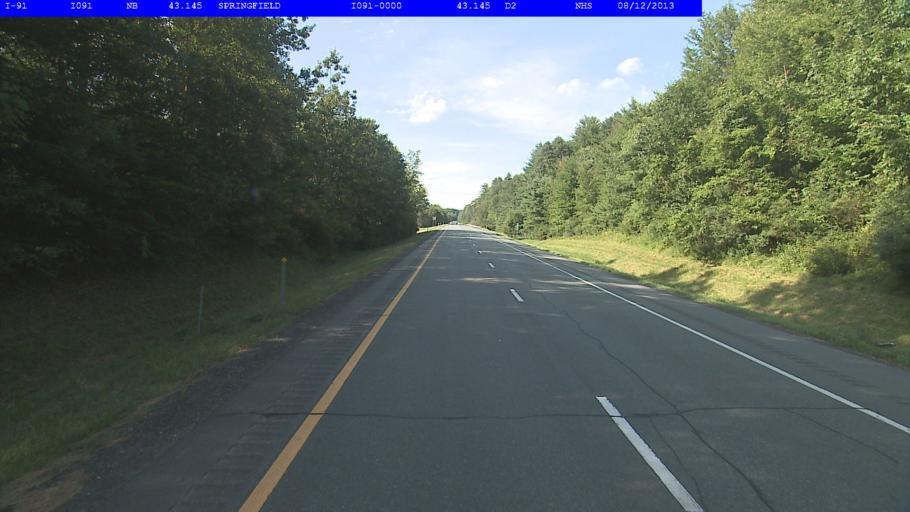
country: US
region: New Hampshire
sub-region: Sullivan County
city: Charlestown
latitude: 43.2862
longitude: -72.4276
